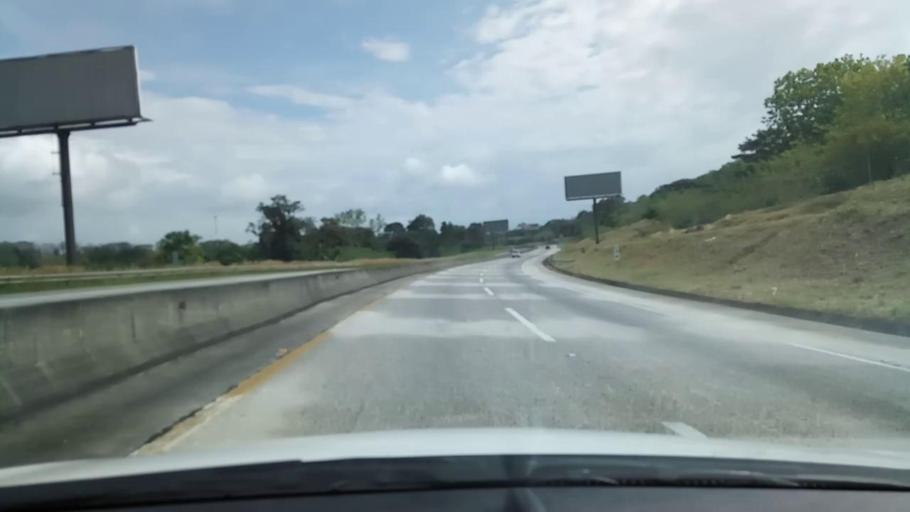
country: PA
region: Colon
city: Buena Vista
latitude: 9.2708
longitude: -79.7077
